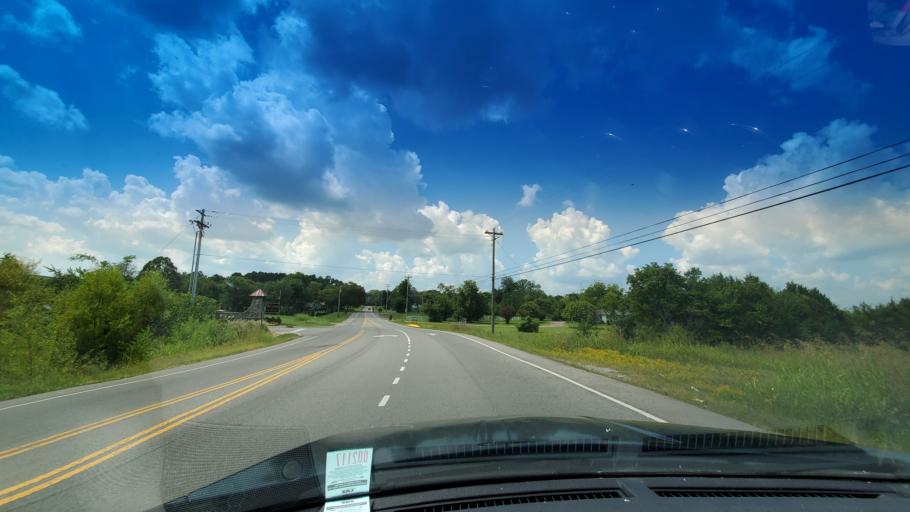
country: US
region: Tennessee
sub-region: Wilson County
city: Lebanon
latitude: 36.1805
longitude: -86.3280
